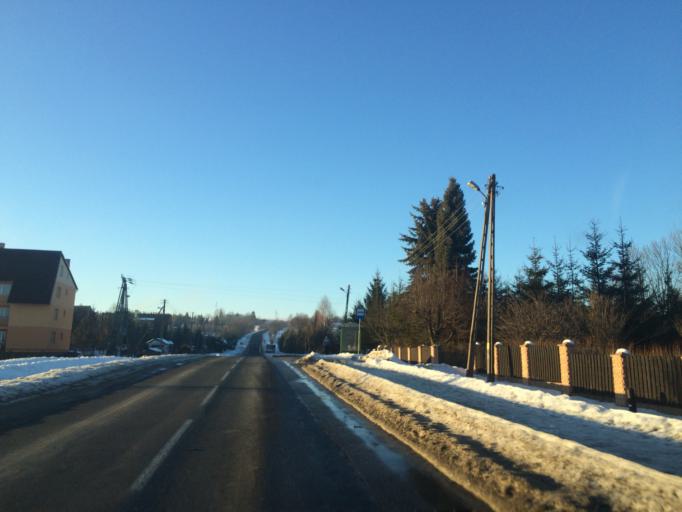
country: PL
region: Subcarpathian Voivodeship
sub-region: Powiat bieszczadzki
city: Lutowiska
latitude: 49.2548
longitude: 22.6898
